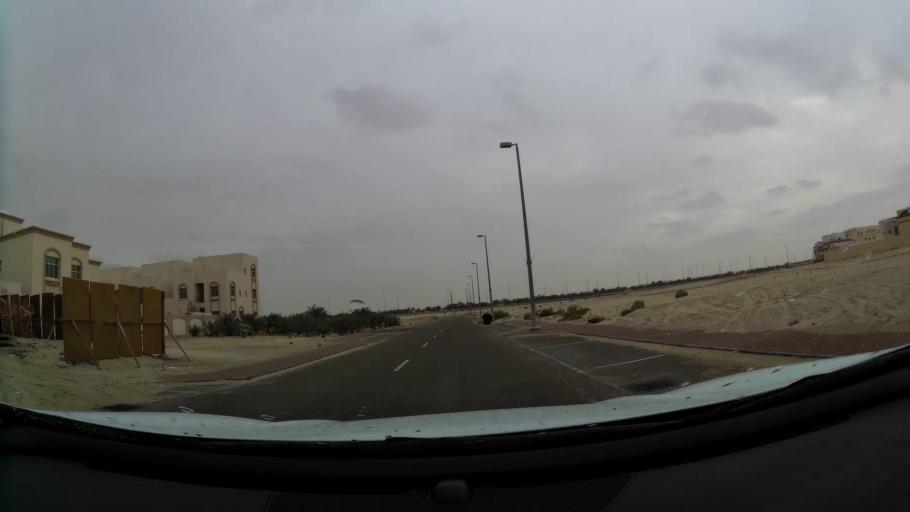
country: AE
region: Abu Dhabi
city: Abu Dhabi
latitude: 24.3656
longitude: 54.6456
